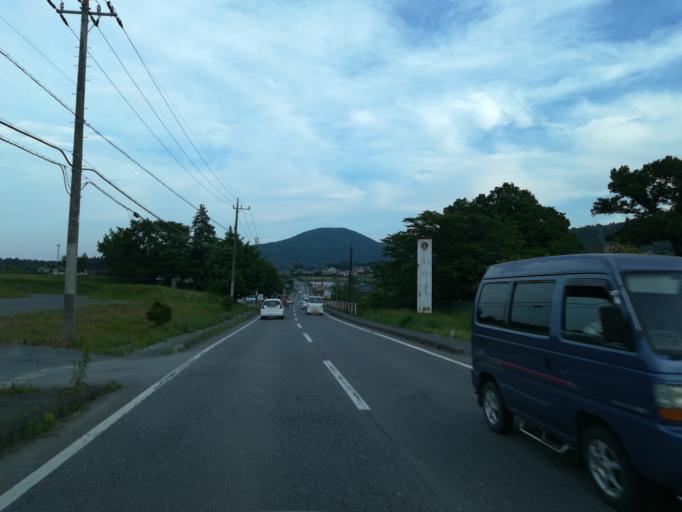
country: JP
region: Ibaraki
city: Tsukuba
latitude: 36.2140
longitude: 140.1726
